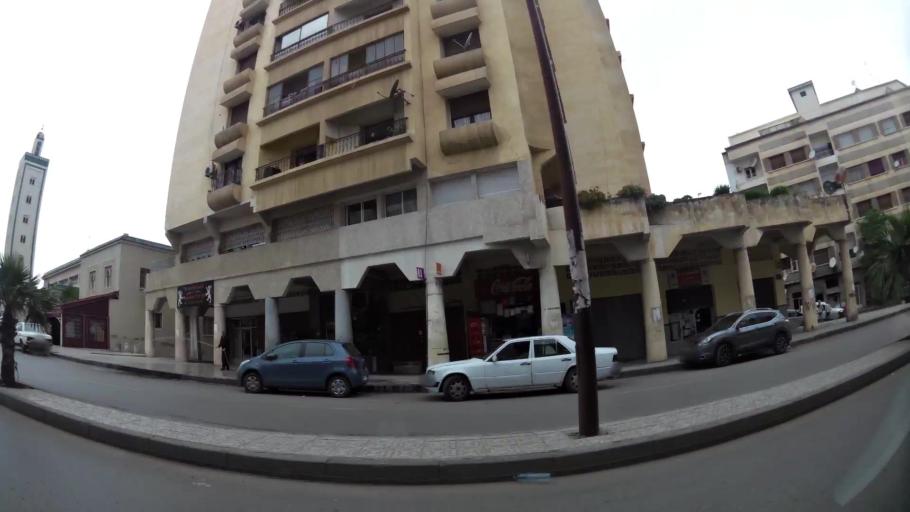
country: MA
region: Fes-Boulemane
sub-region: Fes
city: Fes
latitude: 34.0441
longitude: -5.0056
